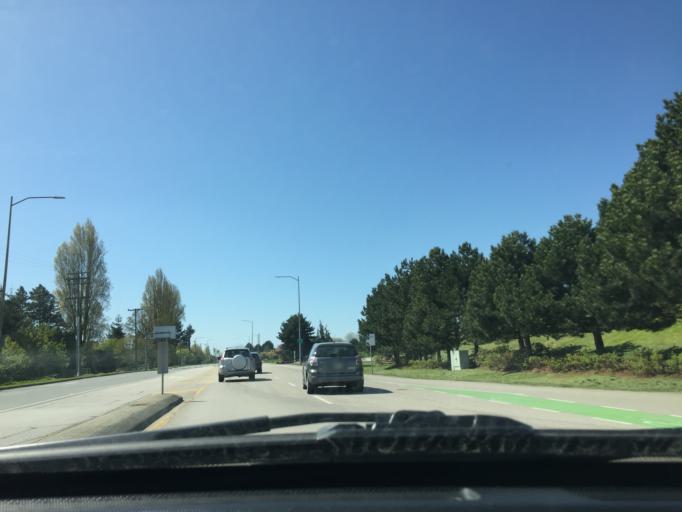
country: CA
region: British Columbia
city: Richmond
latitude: 49.1922
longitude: -123.1426
